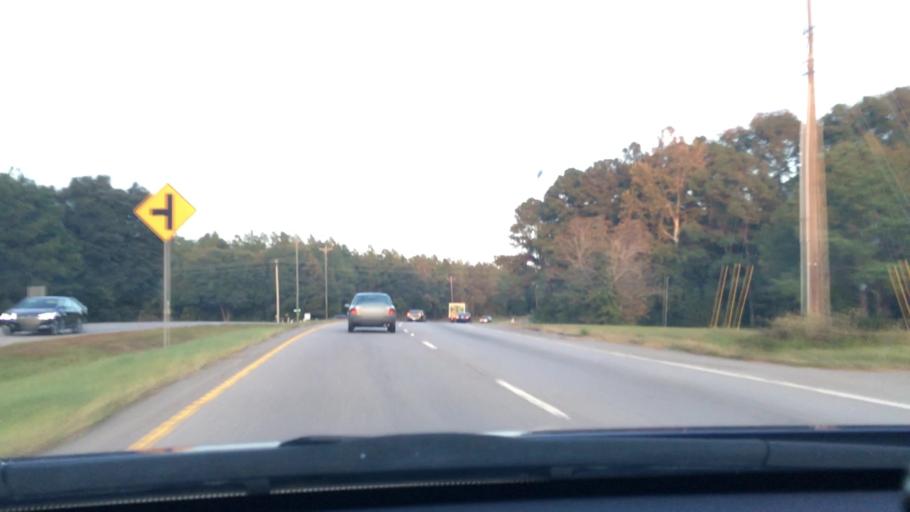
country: US
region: South Carolina
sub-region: Richland County
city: Gadsden
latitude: 33.9425
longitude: -80.7782
